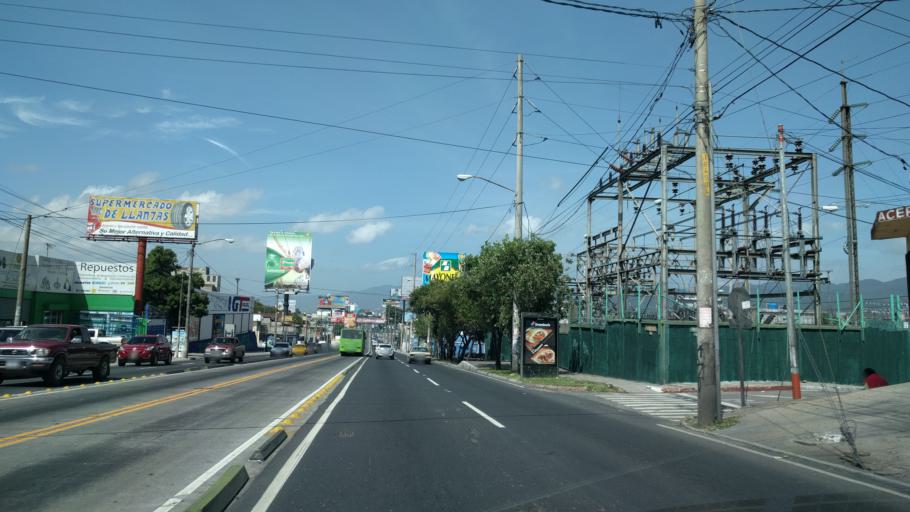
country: GT
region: Guatemala
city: Guatemala City
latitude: 14.6104
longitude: -90.5389
